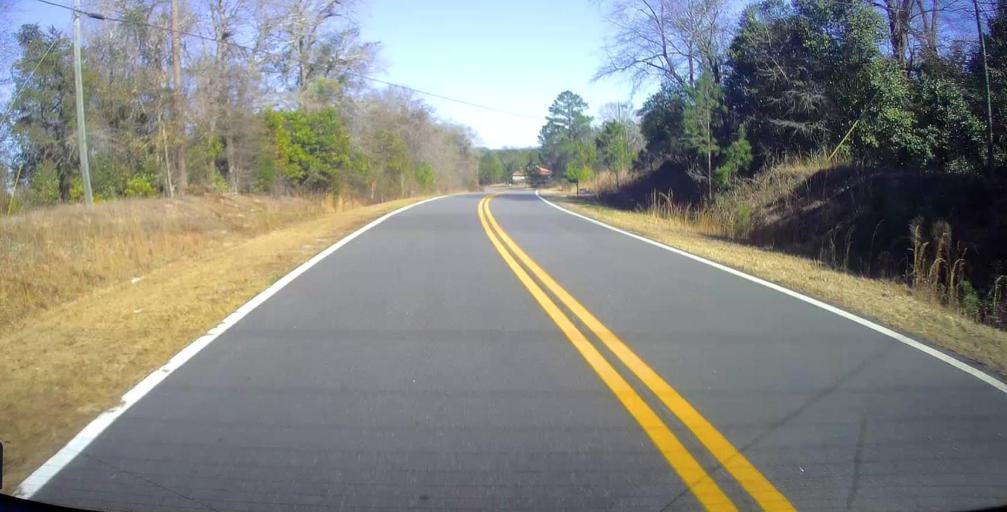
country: US
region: Georgia
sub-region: Peach County
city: Fort Valley
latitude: 32.6444
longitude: -83.9038
